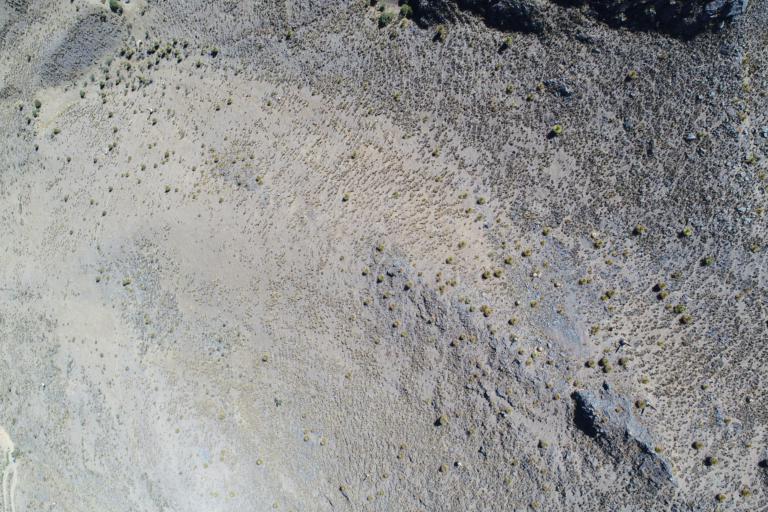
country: BO
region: La Paz
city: Viloco
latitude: -16.8102
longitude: -67.5471
